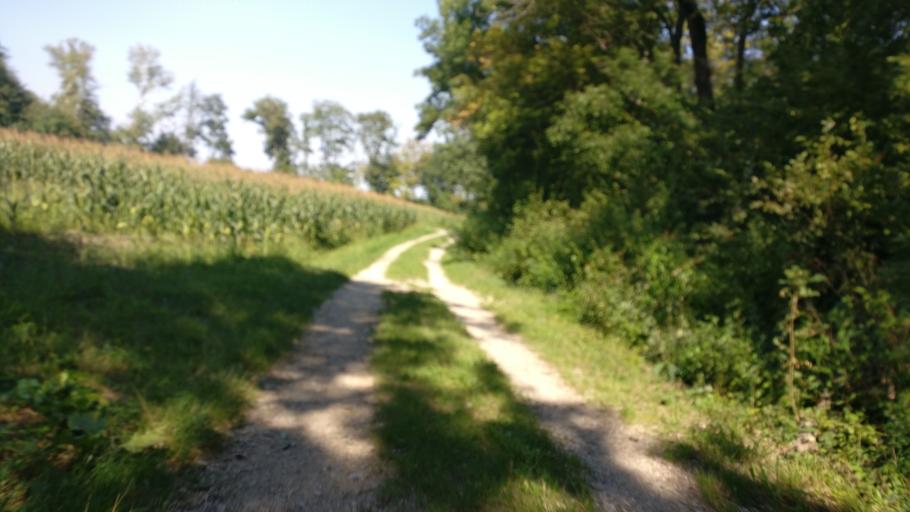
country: AT
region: Lower Austria
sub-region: Politischer Bezirk Baden
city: Mitterndorf an der Fischa
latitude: 47.9724
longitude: 16.4389
